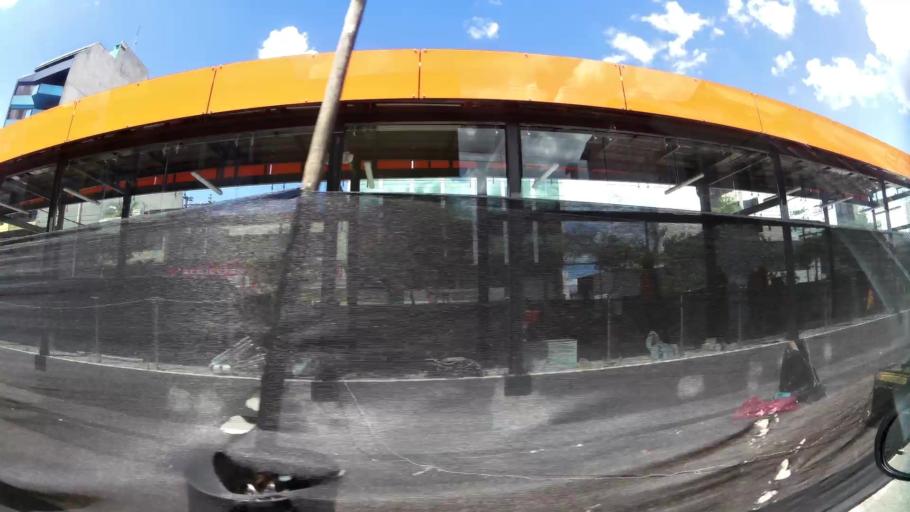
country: EC
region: Pichincha
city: Quito
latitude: -0.1891
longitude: -78.4923
